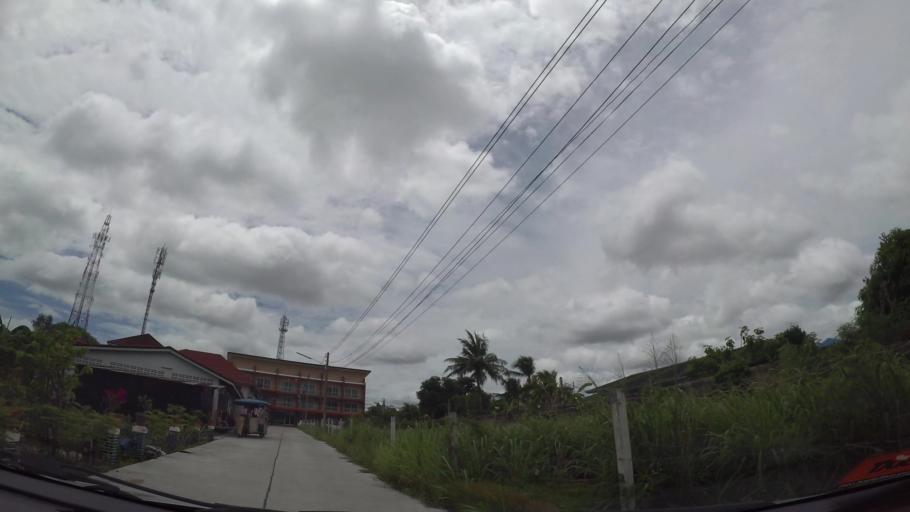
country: TH
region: Chon Buri
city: Sattahip
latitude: 12.7594
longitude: 100.9005
